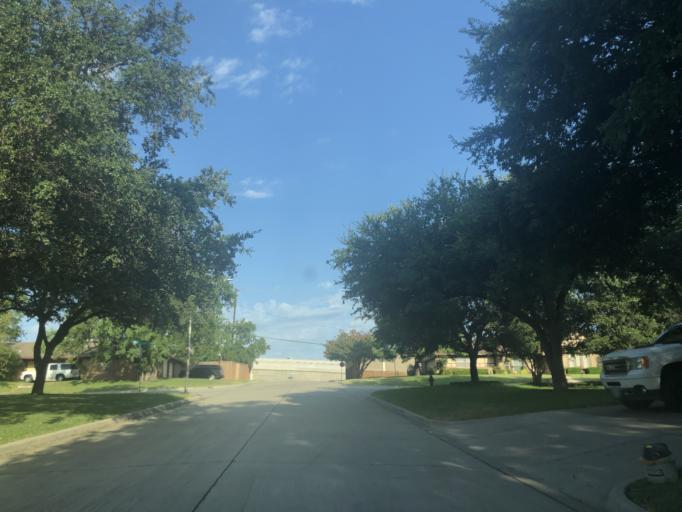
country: US
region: Texas
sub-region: Dallas County
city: Grand Prairie
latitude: 32.7615
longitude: -97.0273
